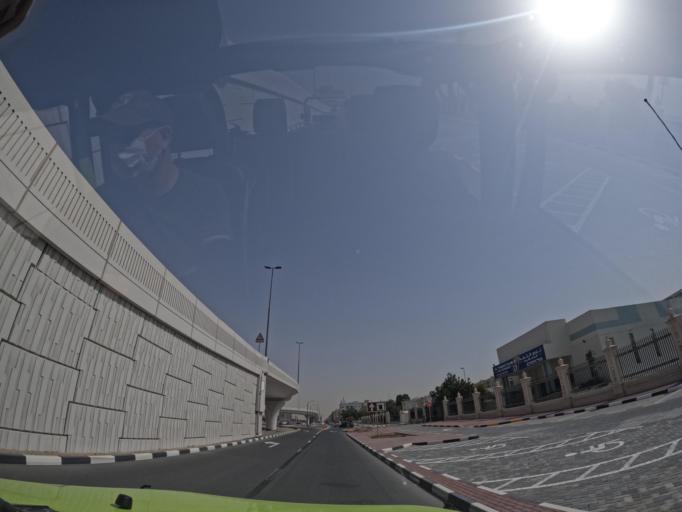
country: AE
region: Ash Shariqah
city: Sharjah
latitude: 25.3142
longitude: 55.4546
